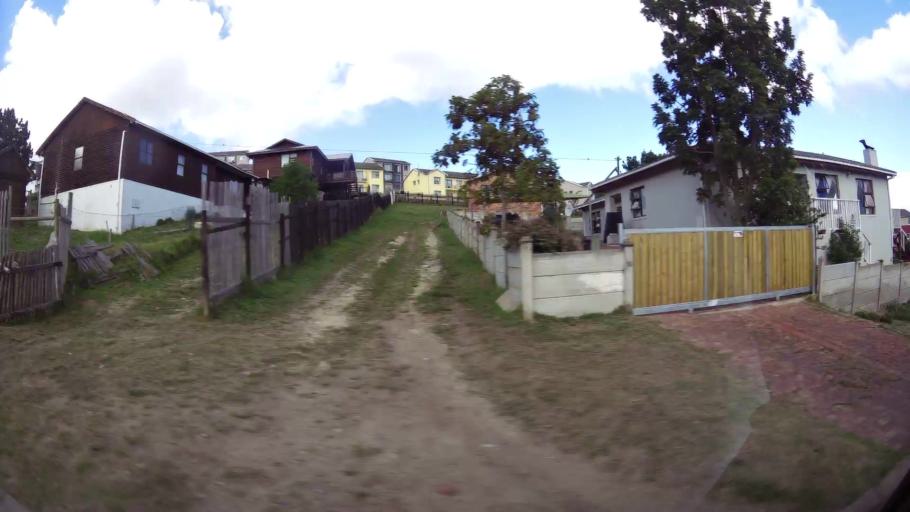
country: ZA
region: Western Cape
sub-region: Eden District Municipality
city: Knysna
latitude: -34.0469
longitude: 23.0858
